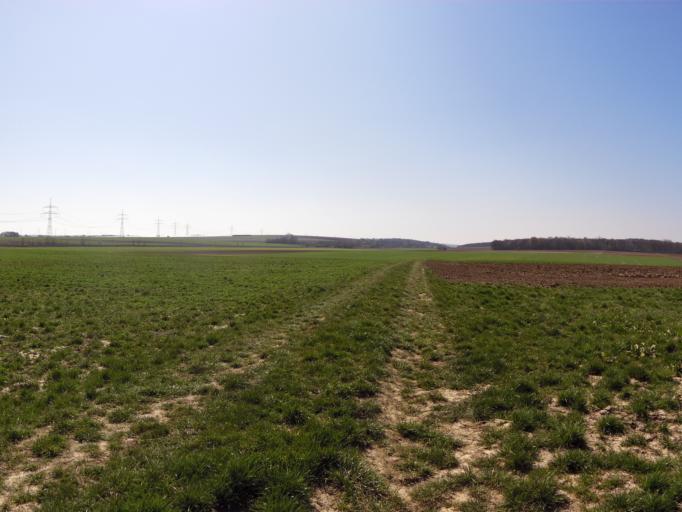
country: DE
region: Bavaria
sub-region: Regierungsbezirk Unterfranken
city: Oberpleichfeld
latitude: 49.8359
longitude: 10.0851
